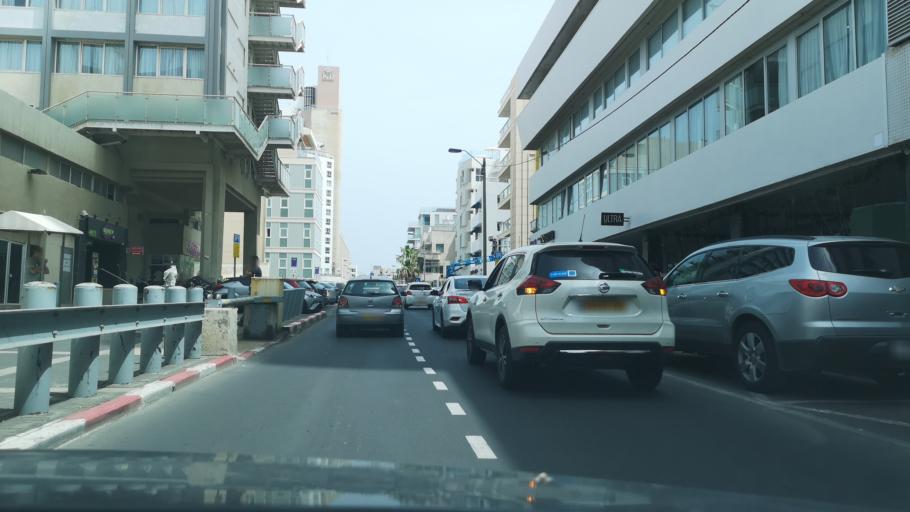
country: IL
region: Tel Aviv
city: Tel Aviv
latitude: 32.0766
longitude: 34.7670
